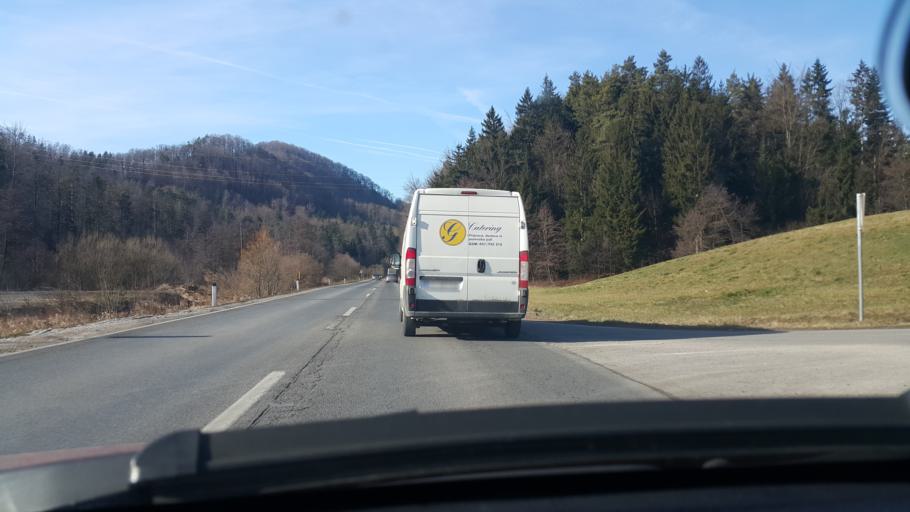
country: SI
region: Velenje
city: Velenje
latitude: 46.3482
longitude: 15.1417
